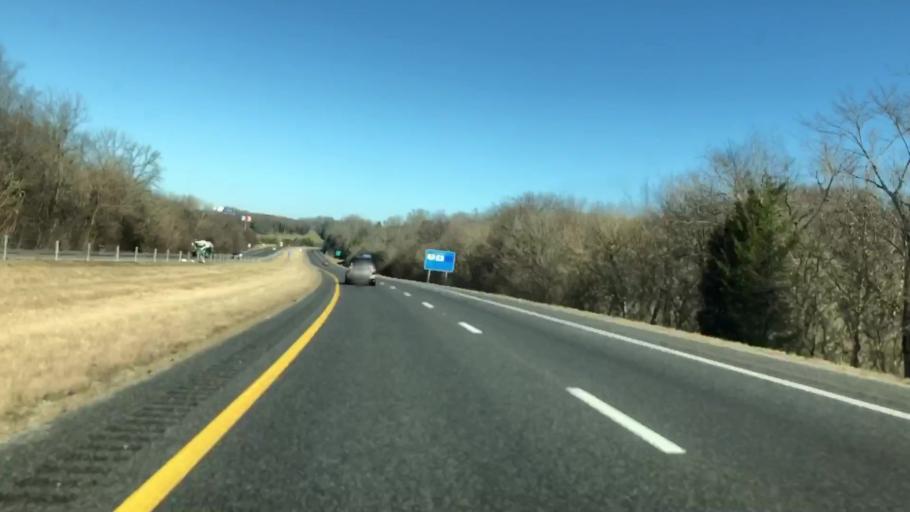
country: US
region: Alabama
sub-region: Limestone County
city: Ardmore
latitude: 35.0002
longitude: -86.8775
